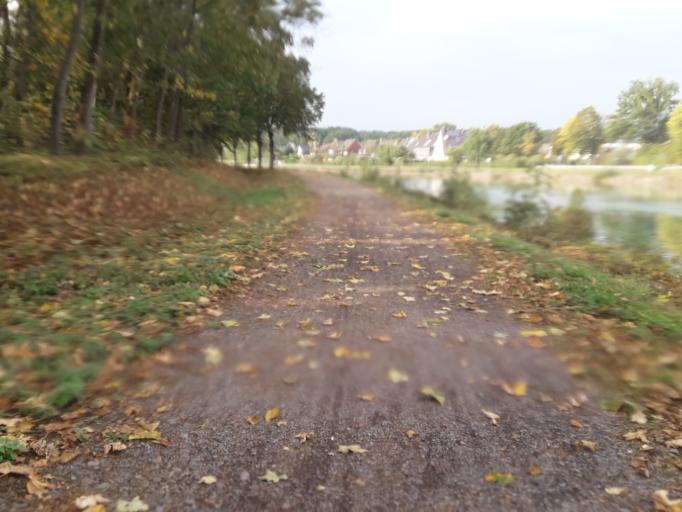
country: DE
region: North Rhine-Westphalia
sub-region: Regierungsbezirk Munster
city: Muenster
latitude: 51.9011
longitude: 7.6593
